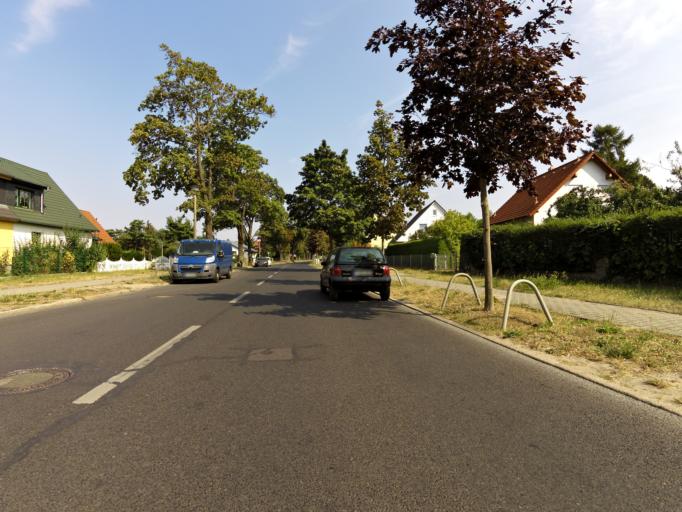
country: DE
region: Berlin
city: Altglienicke
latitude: 52.4187
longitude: 13.5475
